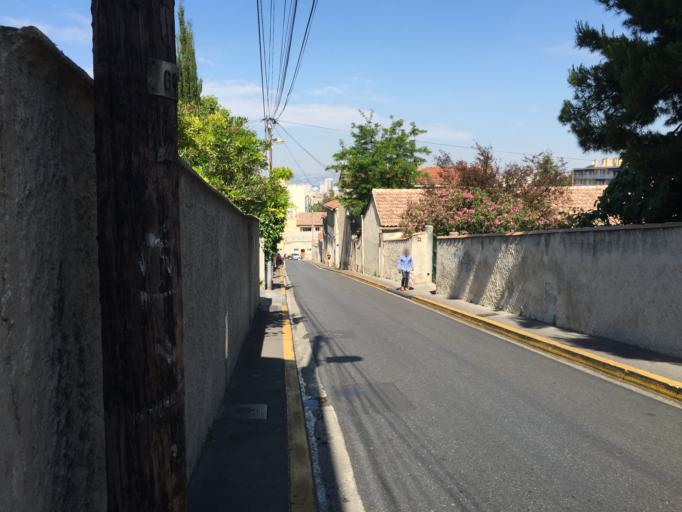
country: FR
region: Provence-Alpes-Cote d'Azur
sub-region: Departement des Bouches-du-Rhone
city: Marseille 04
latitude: 43.3137
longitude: 5.3957
